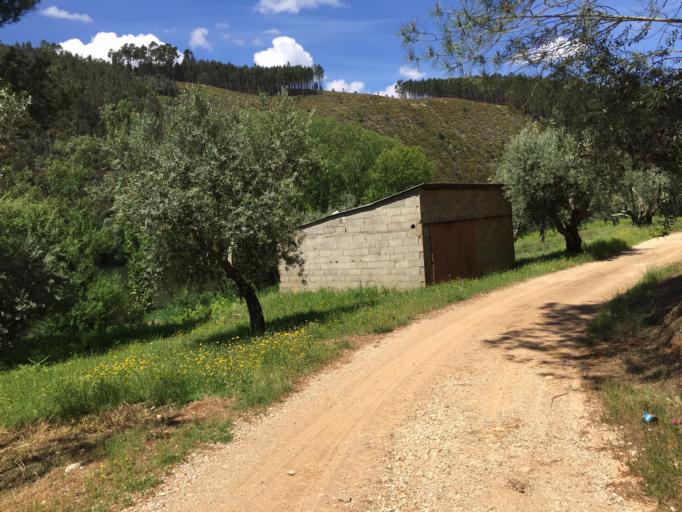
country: PT
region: Coimbra
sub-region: Pampilhosa da Serra
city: Pampilhosa da Serra
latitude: 40.0713
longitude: -7.7827
